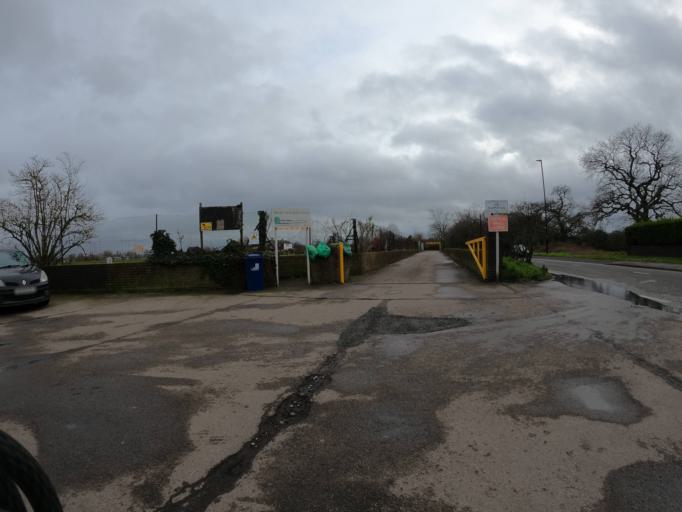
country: GB
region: England
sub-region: Greater London
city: Southall
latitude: 51.5019
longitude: -0.3531
